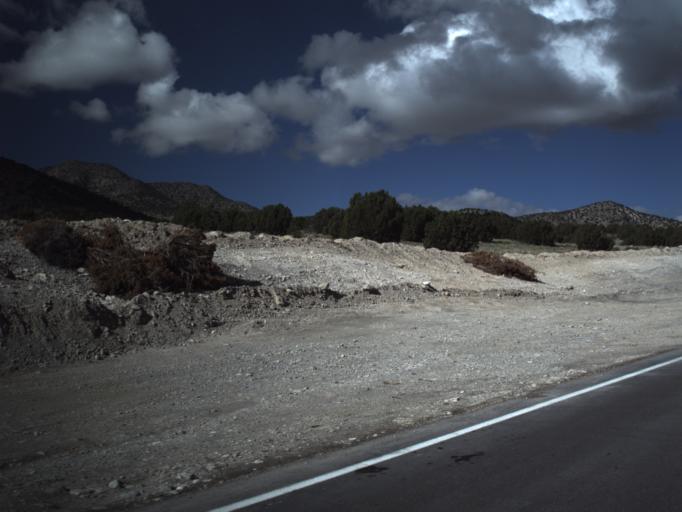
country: US
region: Utah
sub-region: Beaver County
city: Milford
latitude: 38.5076
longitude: -113.5170
